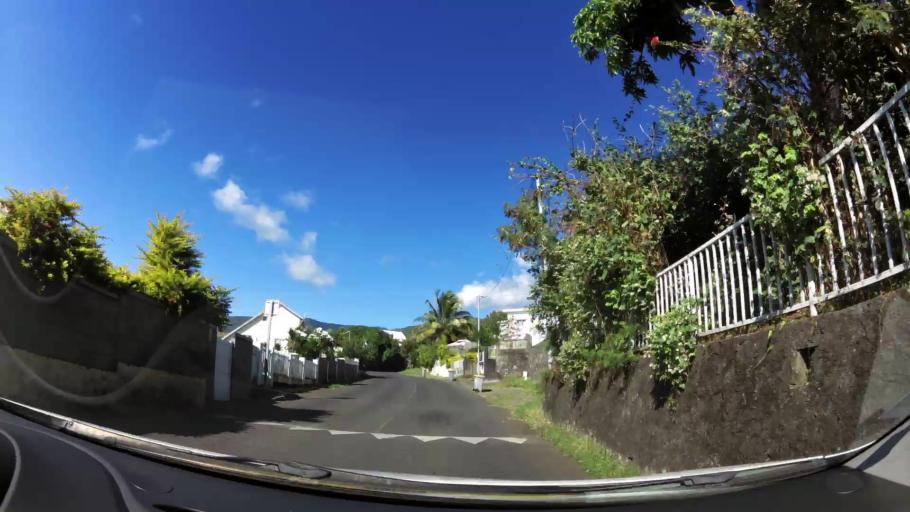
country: RE
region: Reunion
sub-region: Reunion
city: Saint-Denis
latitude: -20.9146
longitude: 55.4835
